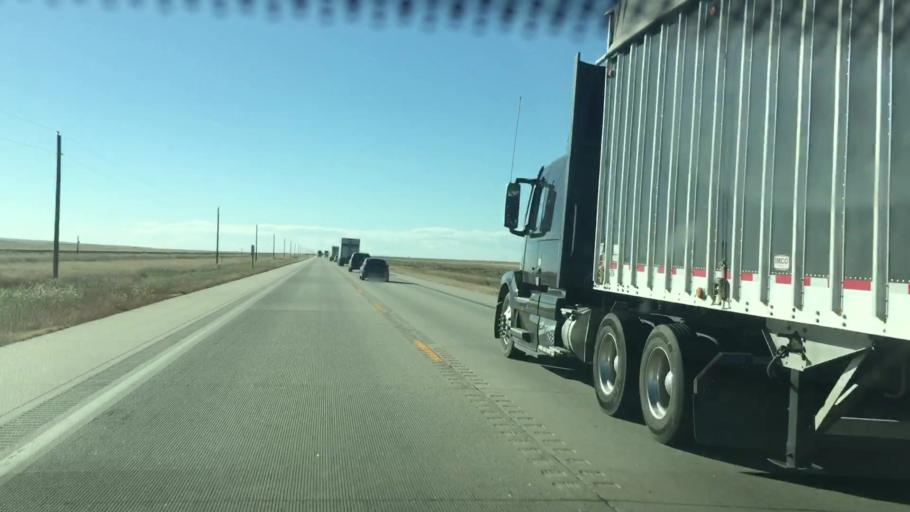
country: US
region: Colorado
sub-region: Kiowa County
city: Eads
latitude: 38.8327
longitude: -103.0536
